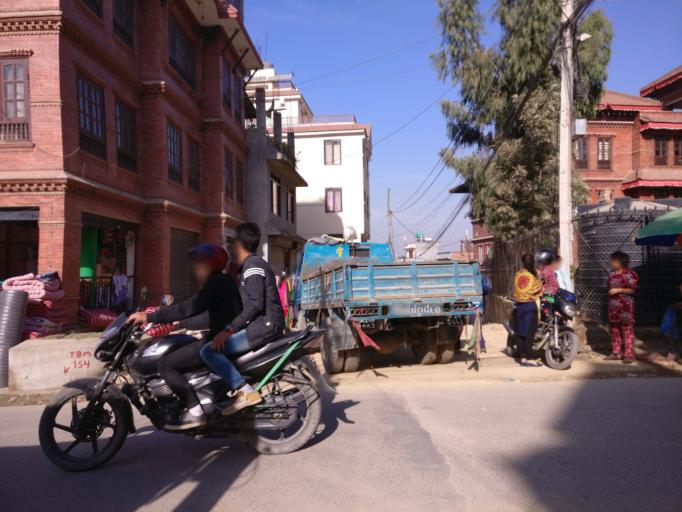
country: NP
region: Central Region
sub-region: Bagmati Zone
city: Patan
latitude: 27.6735
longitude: 85.3315
